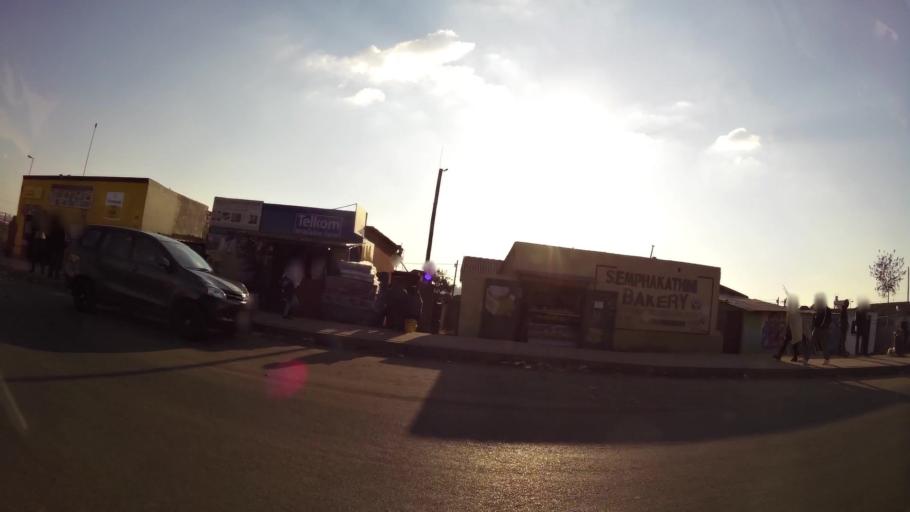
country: ZA
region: Gauteng
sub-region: Ekurhuleni Metropolitan Municipality
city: Tembisa
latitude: -25.9926
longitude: 28.2000
